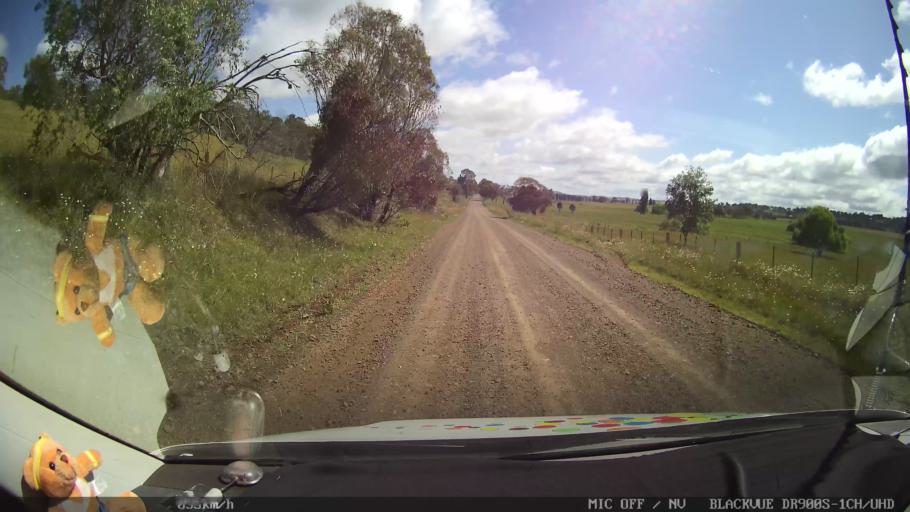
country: AU
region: New South Wales
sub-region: Glen Innes Severn
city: Glen Innes
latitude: -29.9578
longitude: 151.7024
